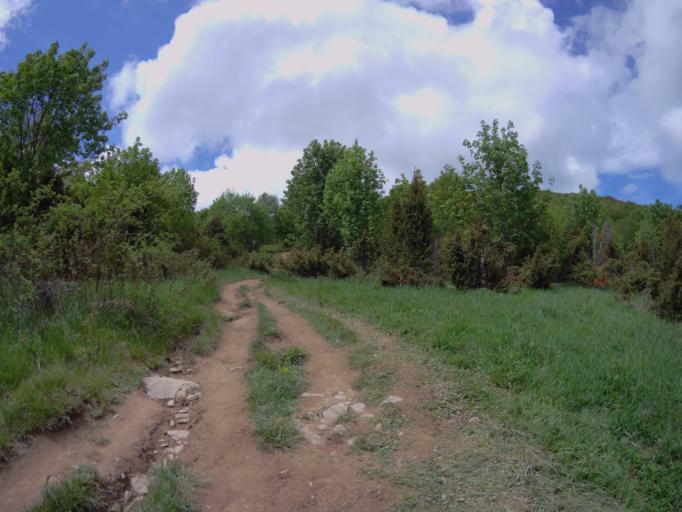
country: PL
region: Subcarpathian Voivodeship
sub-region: Powiat bieszczadzki
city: Lutowiska
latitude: 49.1461
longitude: 22.5620
